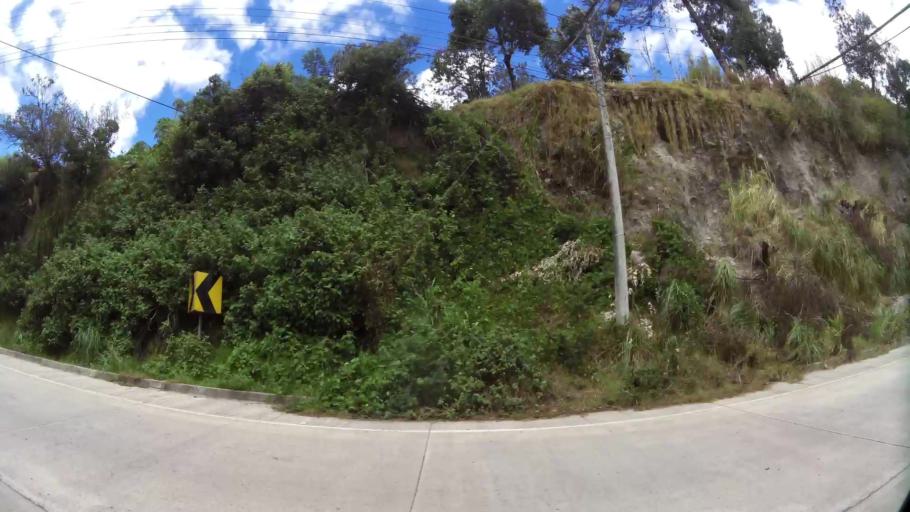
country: EC
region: Azuay
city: Cuenca
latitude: -3.1341
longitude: -79.1324
